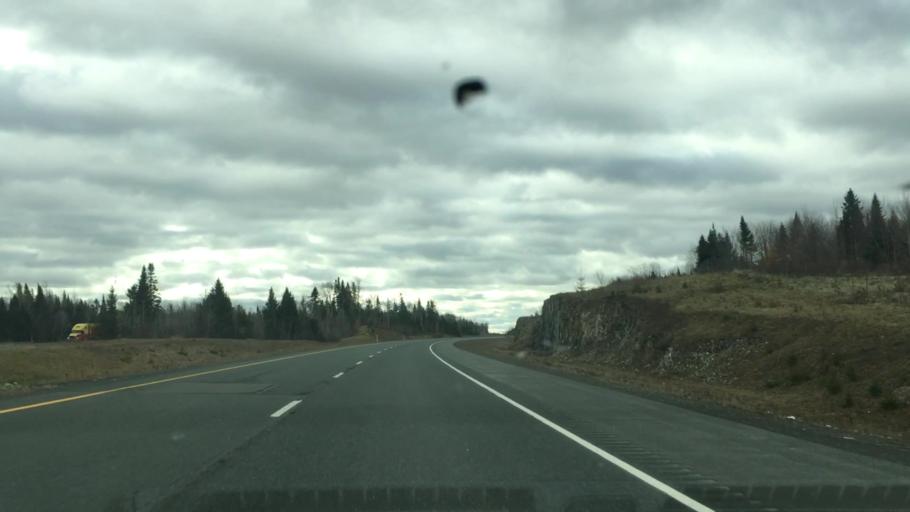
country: US
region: Maine
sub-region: Aroostook County
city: Easton
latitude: 46.6185
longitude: -67.7394
